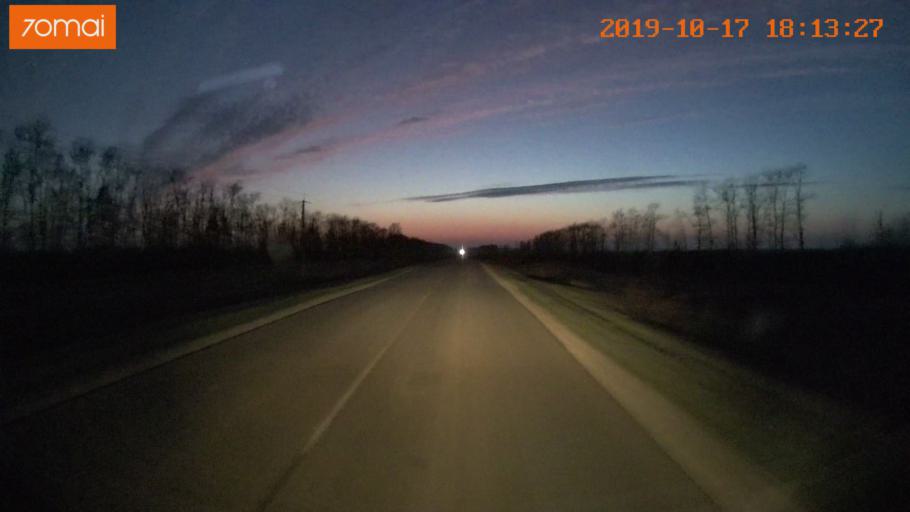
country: RU
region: Tula
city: Kurkino
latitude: 53.4094
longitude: 38.5874
